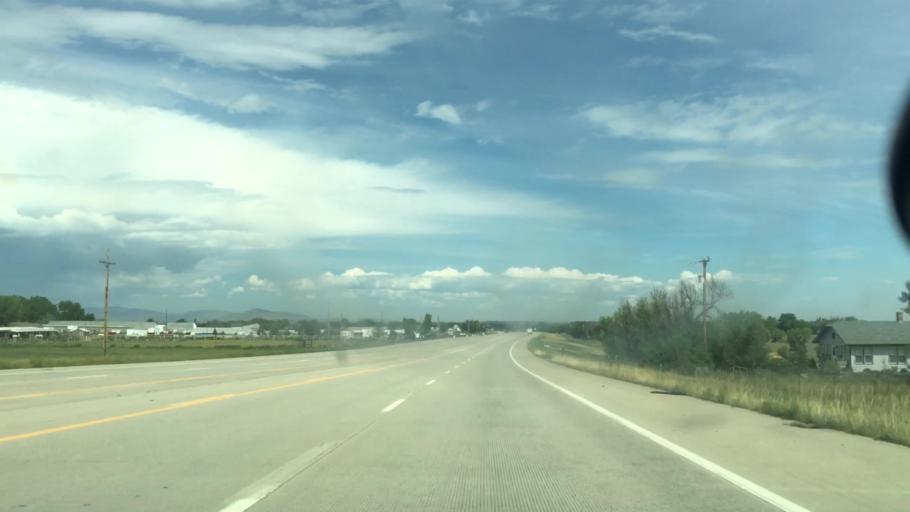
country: US
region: Colorado
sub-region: Larimer County
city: Berthoud
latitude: 40.2535
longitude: -105.1027
